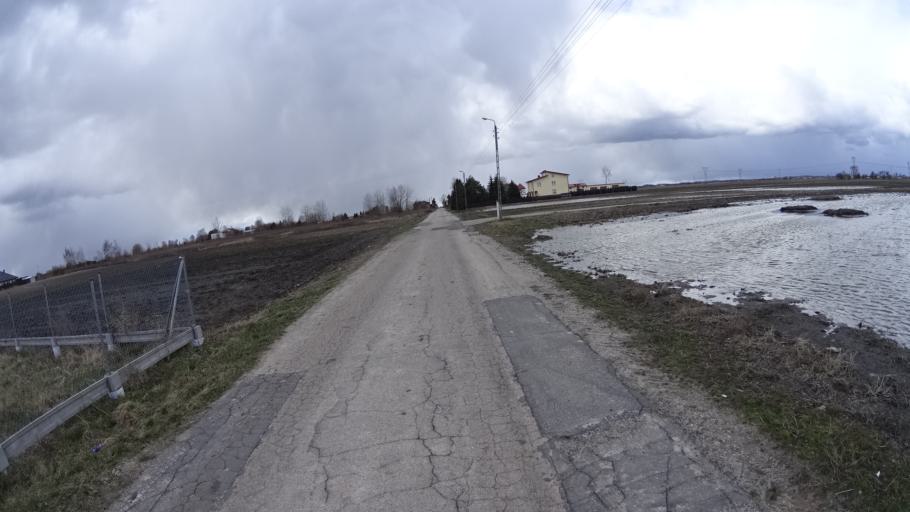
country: PL
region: Masovian Voivodeship
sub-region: Powiat warszawski zachodni
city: Jozefow
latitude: 52.2206
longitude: 20.6894
